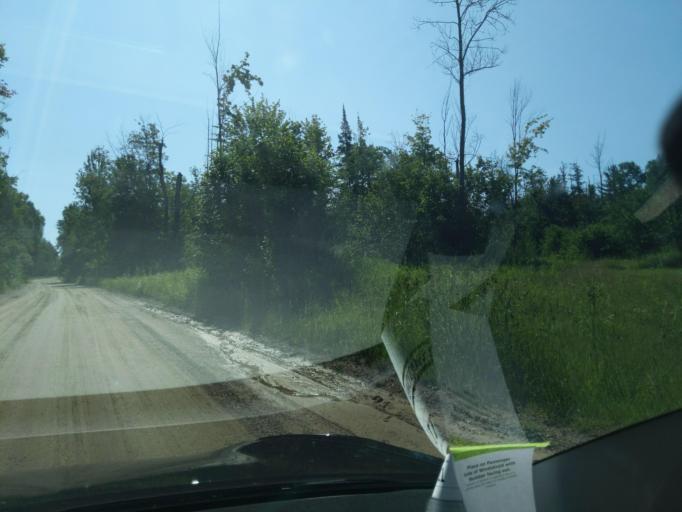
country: US
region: Michigan
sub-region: Mackinac County
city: Saint Ignace
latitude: 45.6794
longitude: -84.6931
